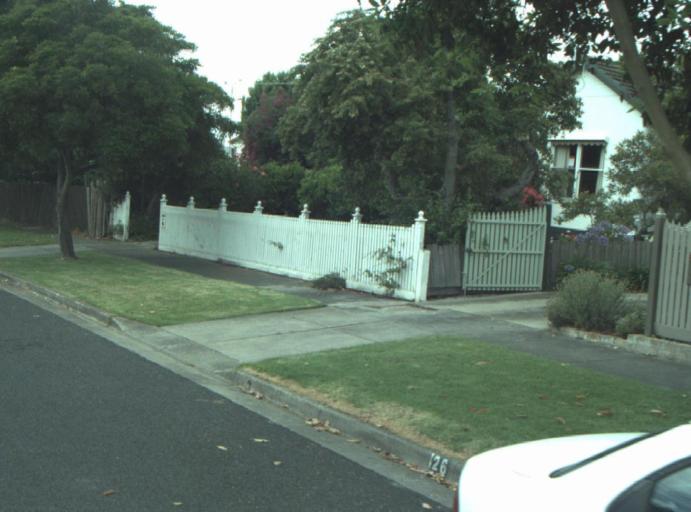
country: AU
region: Victoria
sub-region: Greater Geelong
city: Breakwater
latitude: -38.1753
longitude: 144.3509
